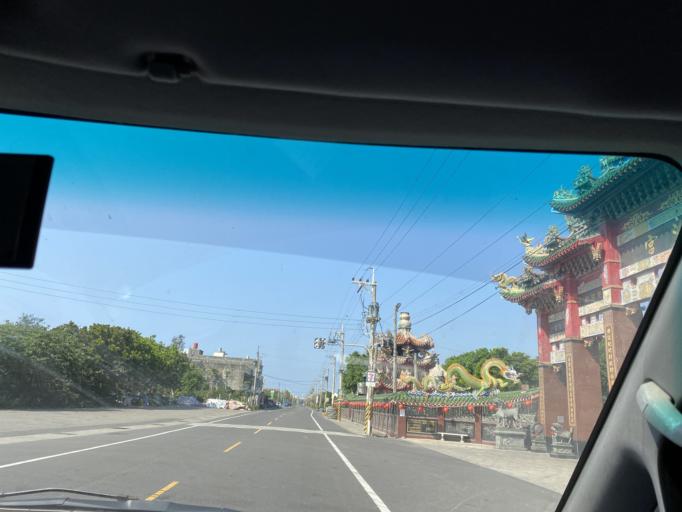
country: TW
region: Taiwan
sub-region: Changhua
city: Chang-hua
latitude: 23.9531
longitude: 120.3338
